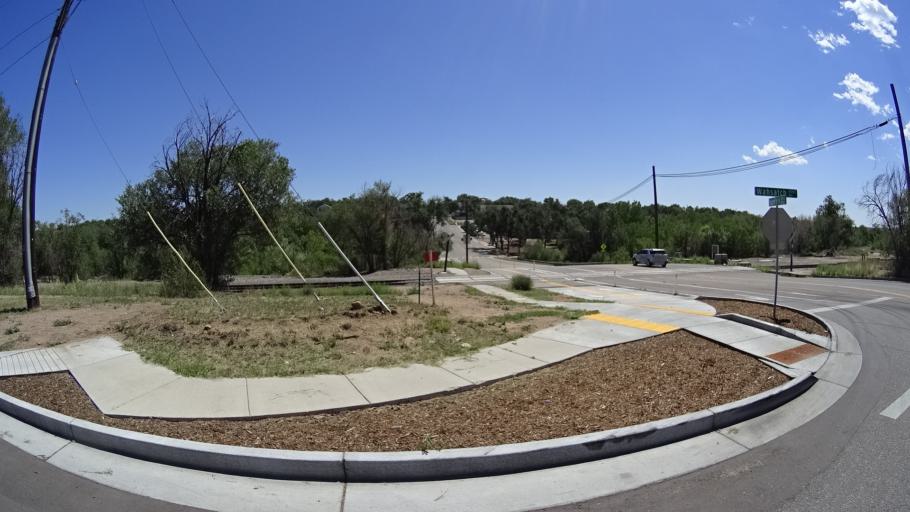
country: US
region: Colorado
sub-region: El Paso County
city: Colorado Springs
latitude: 38.8217
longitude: -104.8186
